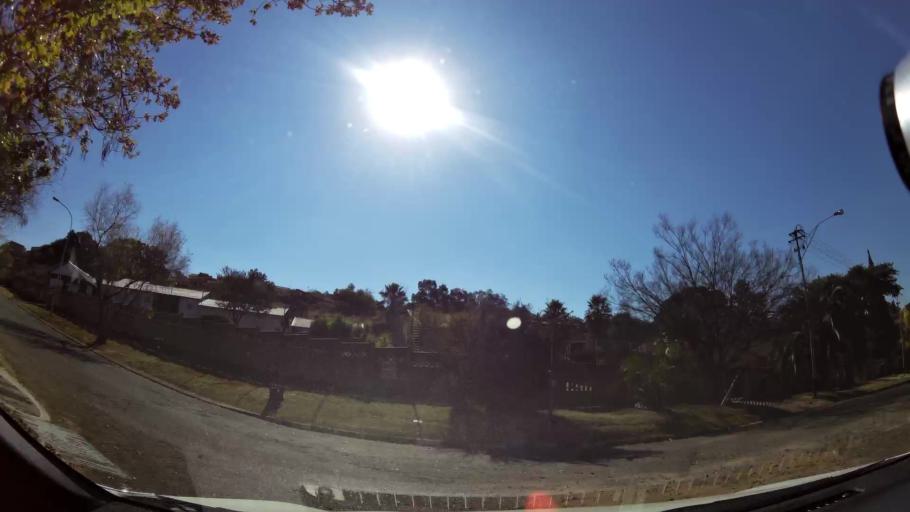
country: ZA
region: Gauteng
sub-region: City of Johannesburg Metropolitan Municipality
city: Johannesburg
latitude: -26.2683
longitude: 28.0239
